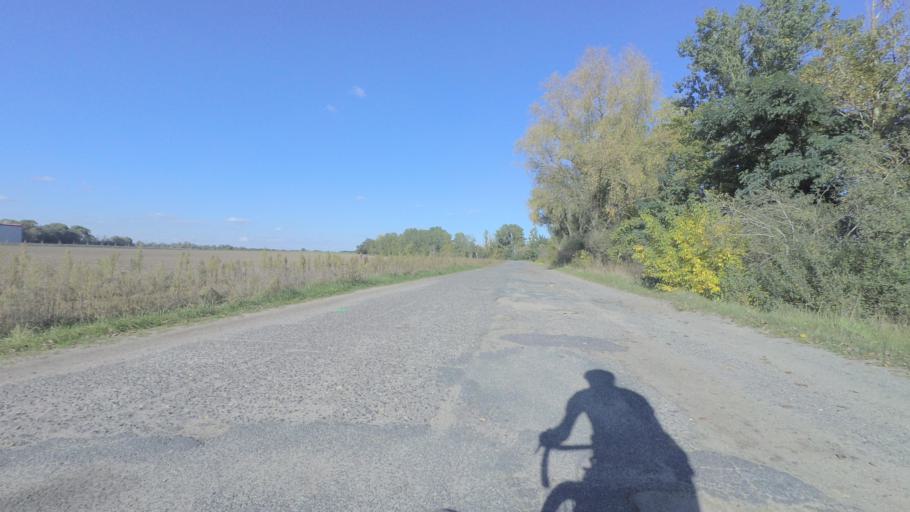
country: DE
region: Brandenburg
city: Rangsdorf
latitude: 52.2932
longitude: 13.4754
